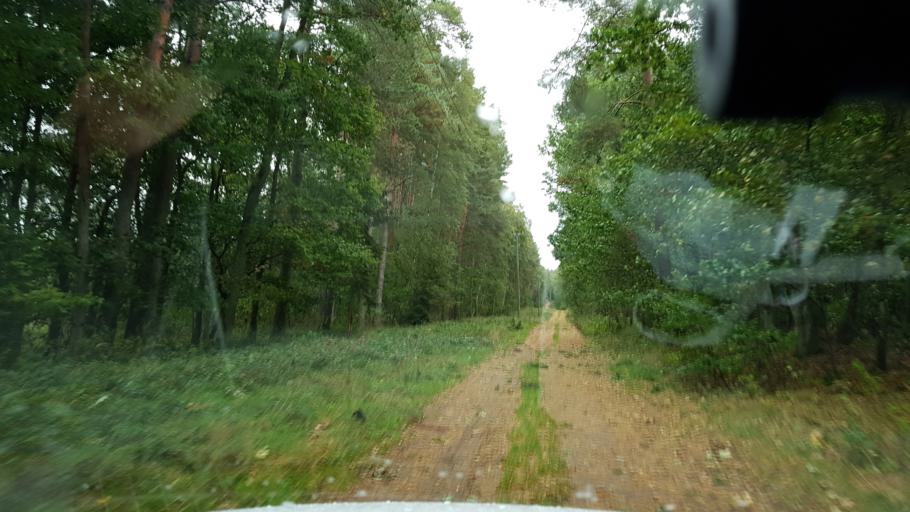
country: PL
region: West Pomeranian Voivodeship
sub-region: Powiat goleniowski
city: Przybiernow
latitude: 53.7507
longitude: 14.7479
